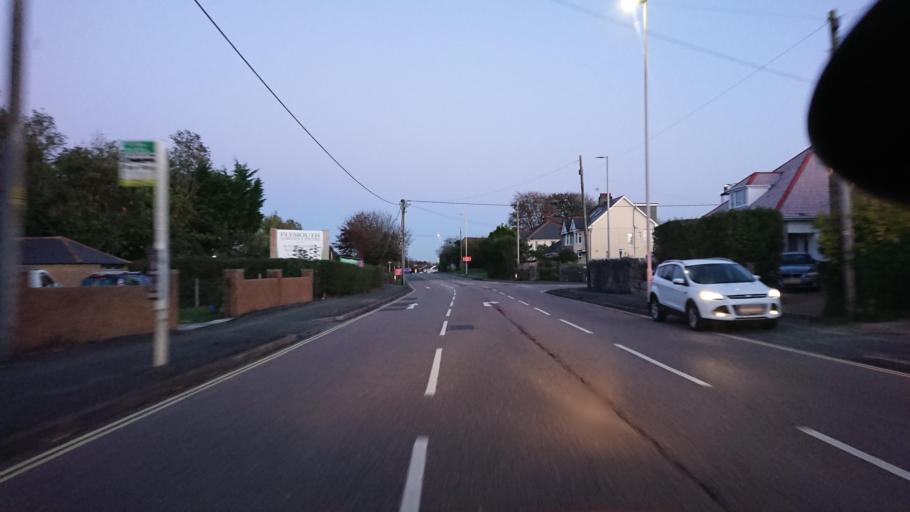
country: GB
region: England
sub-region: Plymouth
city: Plymouth
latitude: 50.4054
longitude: -4.1196
